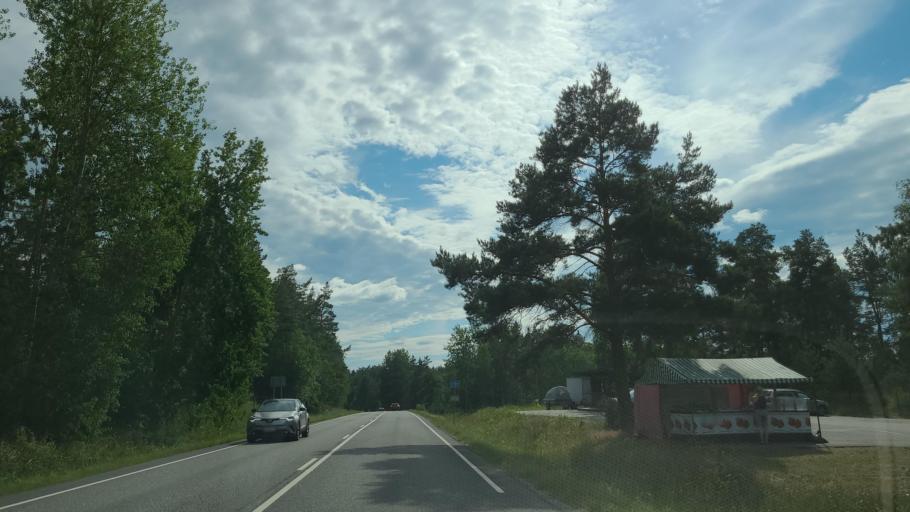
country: FI
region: Varsinais-Suomi
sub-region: Turku
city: Merimasku
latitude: 60.4496
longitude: 21.9009
